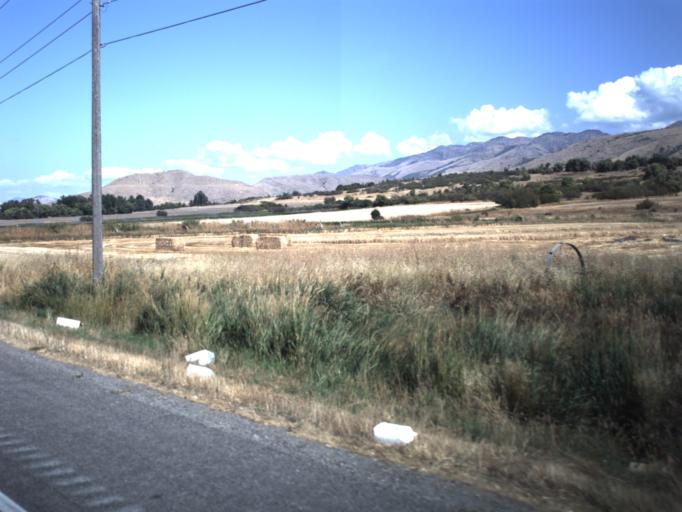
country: US
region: Utah
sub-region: Cache County
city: Richmond
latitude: 41.9313
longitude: -111.8140
